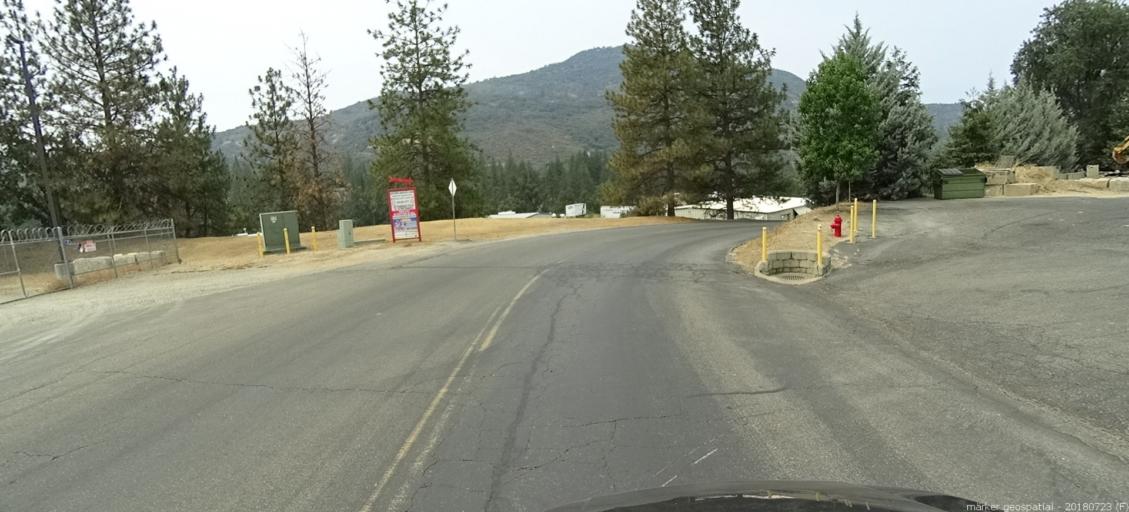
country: US
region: California
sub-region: Madera County
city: Oakhurst
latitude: 37.3320
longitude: -119.6615
